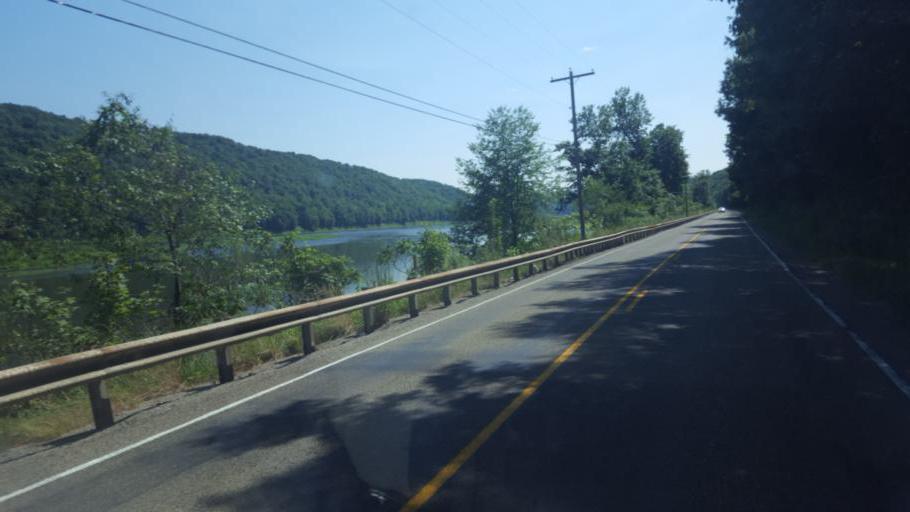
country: US
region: Pennsylvania
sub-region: Butler County
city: Chicora
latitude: 41.1138
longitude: -79.6800
